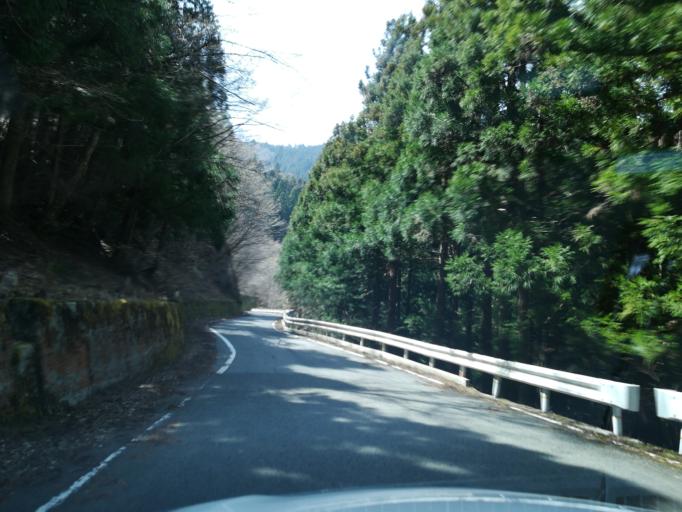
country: JP
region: Tokushima
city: Wakimachi
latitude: 33.8857
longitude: 134.0491
